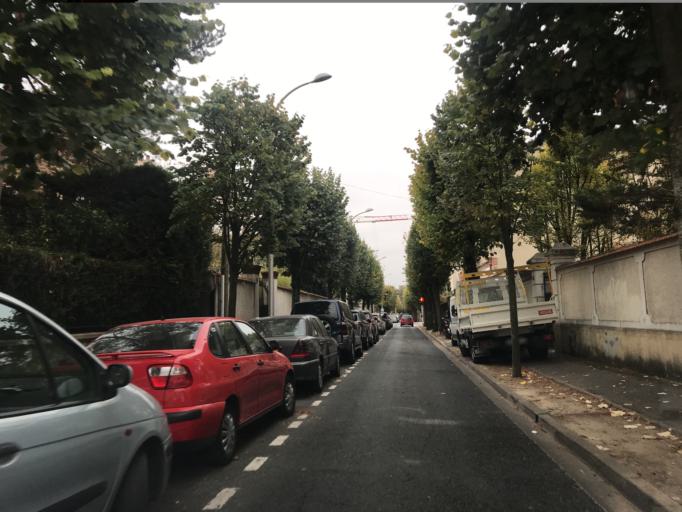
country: FR
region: Ile-de-France
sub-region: Departement du Val-de-Marne
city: Bry-sur-Marne
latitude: 48.8355
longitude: 2.5106
